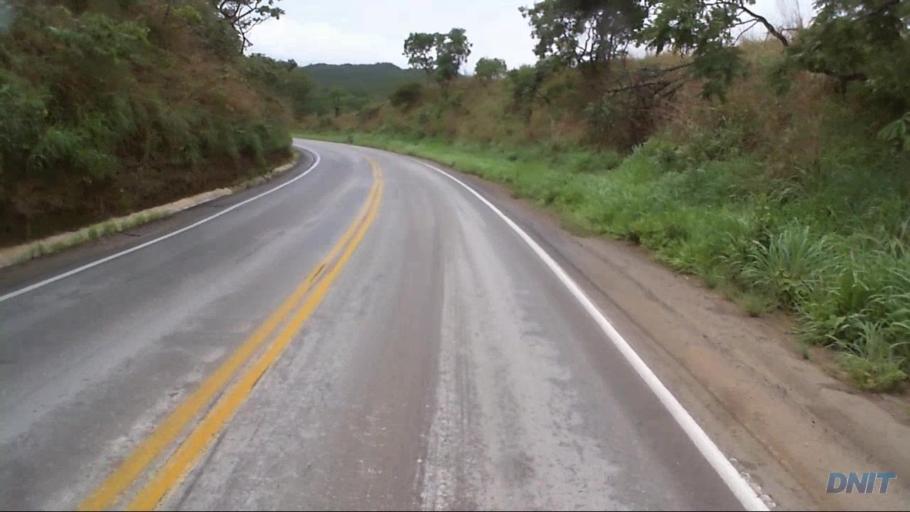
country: BR
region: Goias
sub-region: Padre Bernardo
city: Padre Bernardo
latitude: -15.4826
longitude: -48.2351
